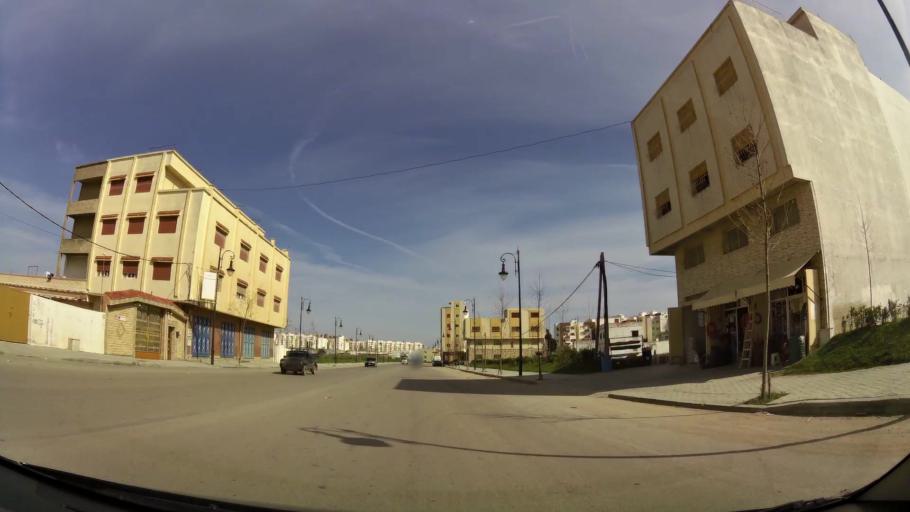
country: MA
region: Tanger-Tetouan
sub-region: Tanger-Assilah
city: Tangier
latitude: 35.7172
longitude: -5.8044
